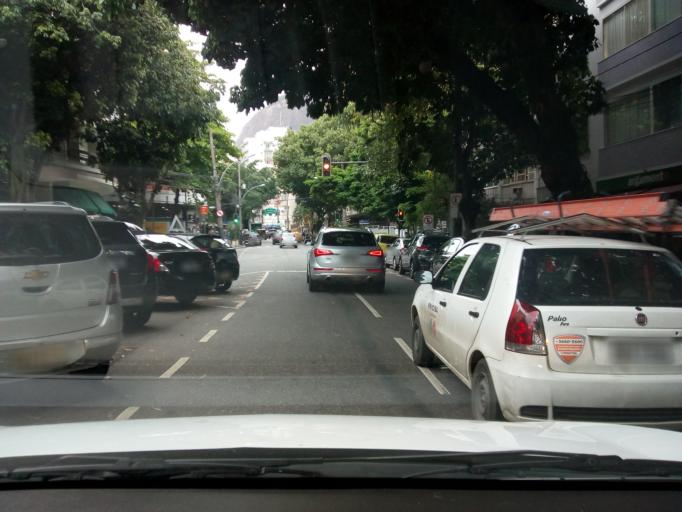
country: BR
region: Rio de Janeiro
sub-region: Rio De Janeiro
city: Rio de Janeiro
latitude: -22.9828
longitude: -43.2261
